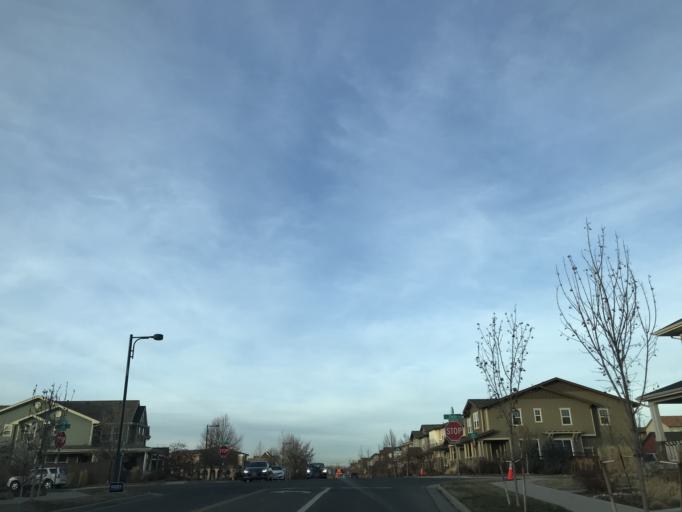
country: US
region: Colorado
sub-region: Adams County
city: Aurora
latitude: 39.7541
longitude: -104.8646
